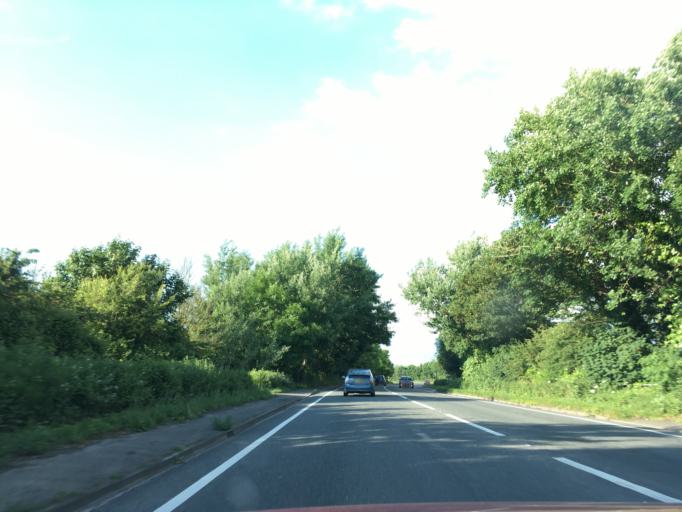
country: GB
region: England
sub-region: Somerset
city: Highbridge
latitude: 51.2508
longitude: -2.9368
